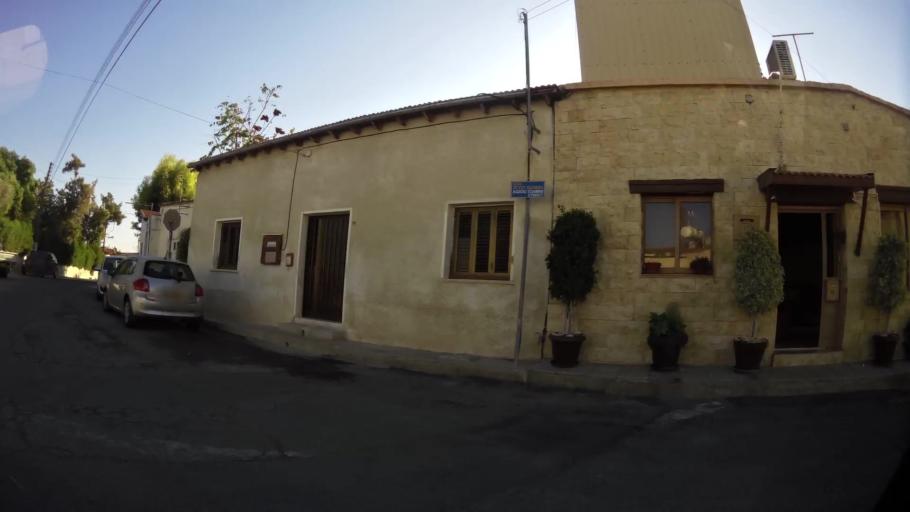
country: CY
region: Larnaka
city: Larnaca
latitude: 34.9240
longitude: 33.6241
